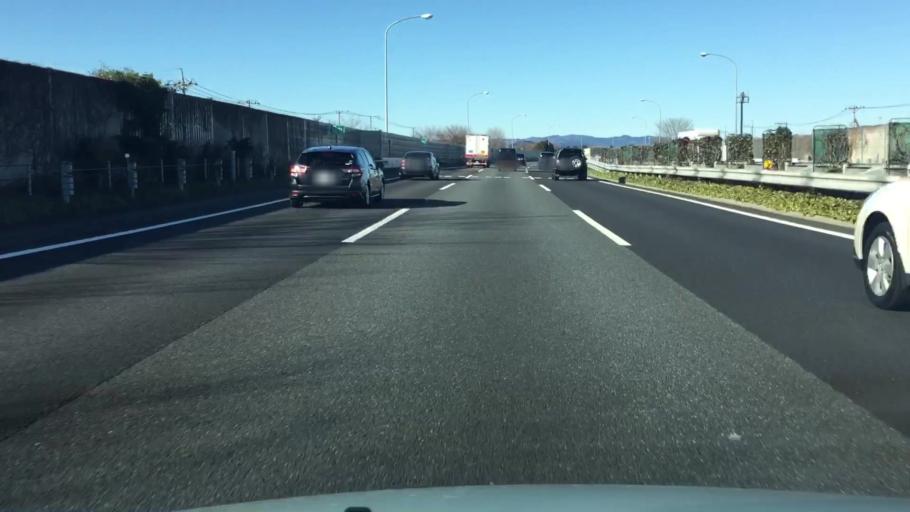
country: JP
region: Saitama
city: Ogawa
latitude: 36.0443
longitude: 139.3553
